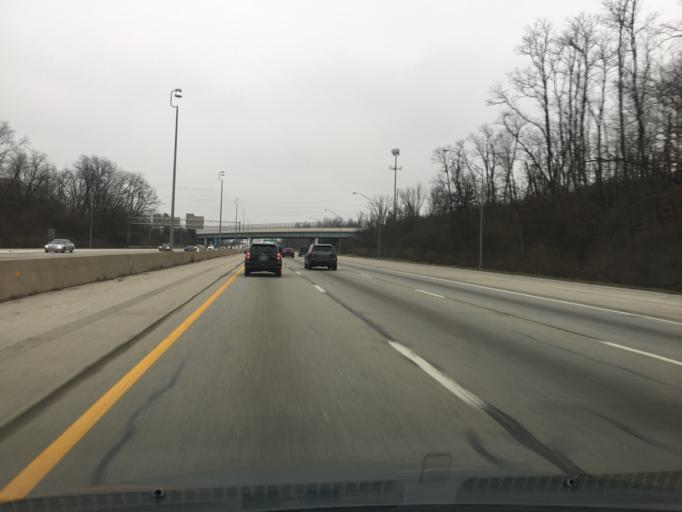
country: US
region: Ohio
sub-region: Hamilton County
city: Highpoint
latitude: 39.2841
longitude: -84.3689
